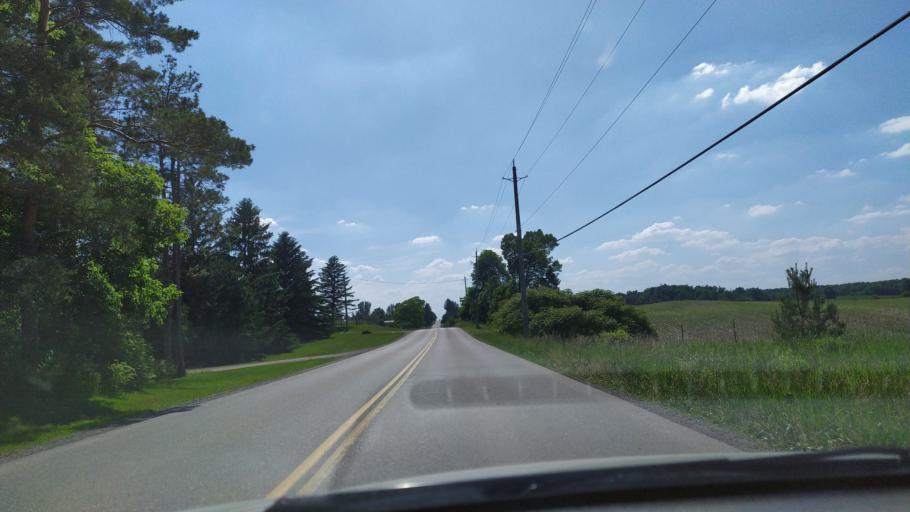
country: CA
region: Ontario
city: Kitchener
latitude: 43.3680
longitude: -80.5792
